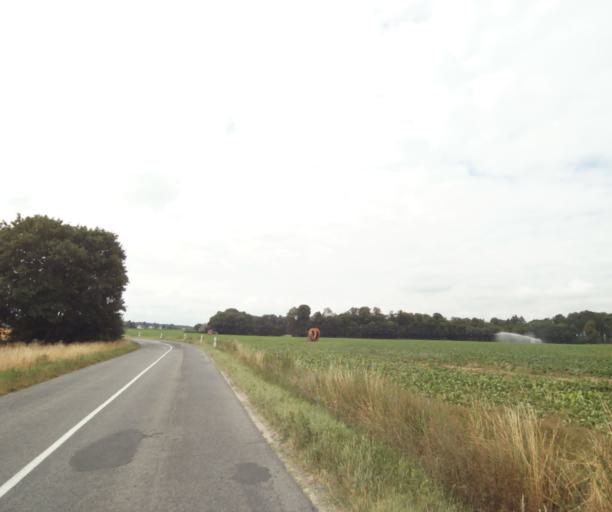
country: FR
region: Centre
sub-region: Departement du Loiret
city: Vennecy
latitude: 47.9313
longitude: 2.0444
